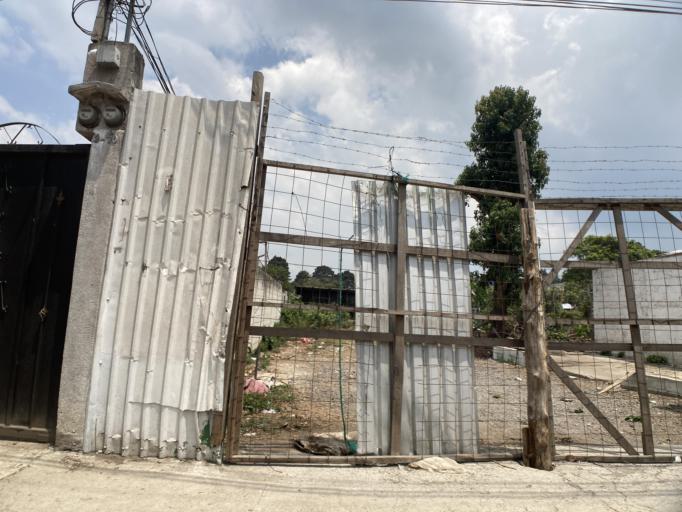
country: GT
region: Guatemala
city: Villa Canales
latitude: 14.4073
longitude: -90.5440
